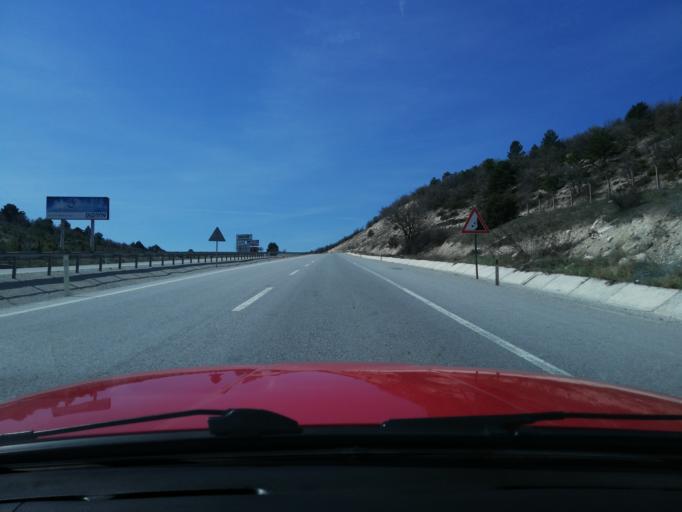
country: TR
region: Kuetahya
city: Kutahya
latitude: 39.3640
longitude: 30.0630
